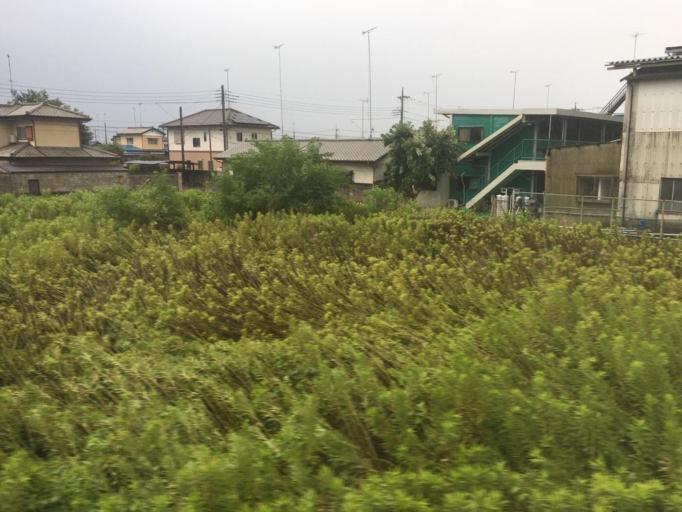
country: JP
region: Tochigi
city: Ashikaga
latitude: 36.3202
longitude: 139.4219
